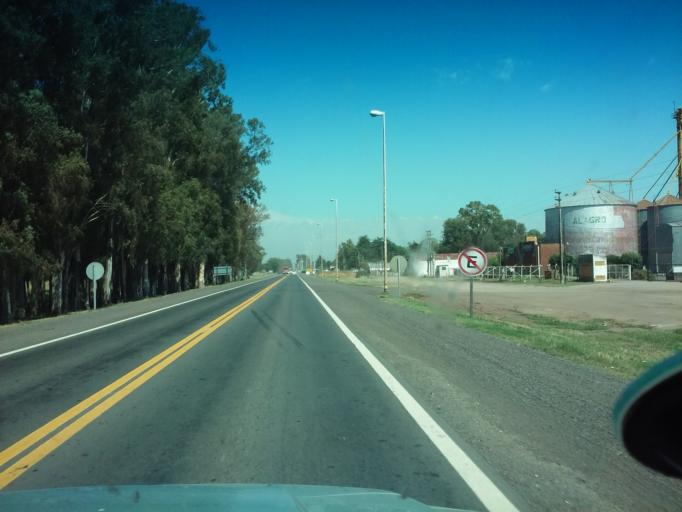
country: AR
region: Buenos Aires
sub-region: Partido de Nueve de Julio
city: Nueve de Julio
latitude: -35.4724
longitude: -60.8579
